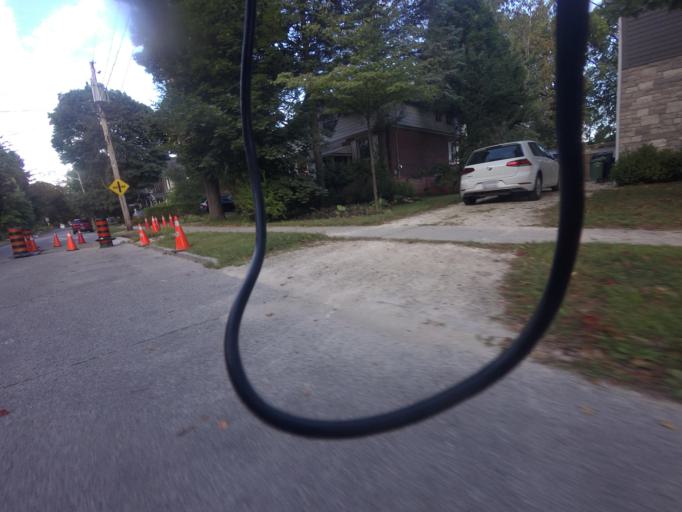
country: CA
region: Ontario
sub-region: Wellington County
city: Guelph
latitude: 43.5428
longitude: -80.2619
